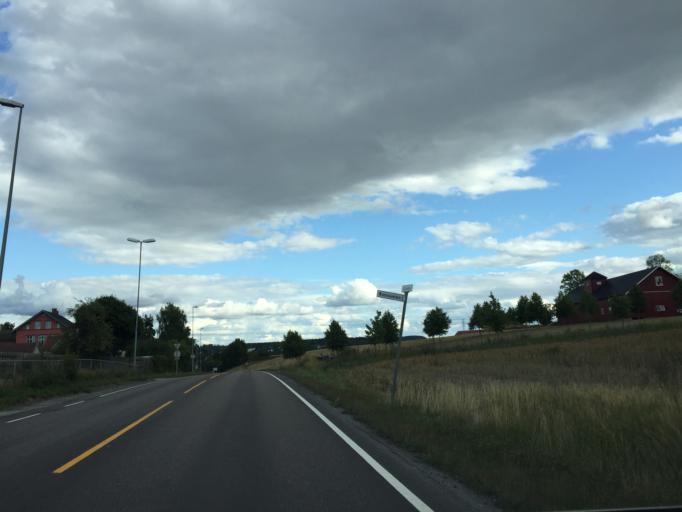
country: NO
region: Ostfold
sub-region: Askim
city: Askim
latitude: 59.5865
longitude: 11.1212
